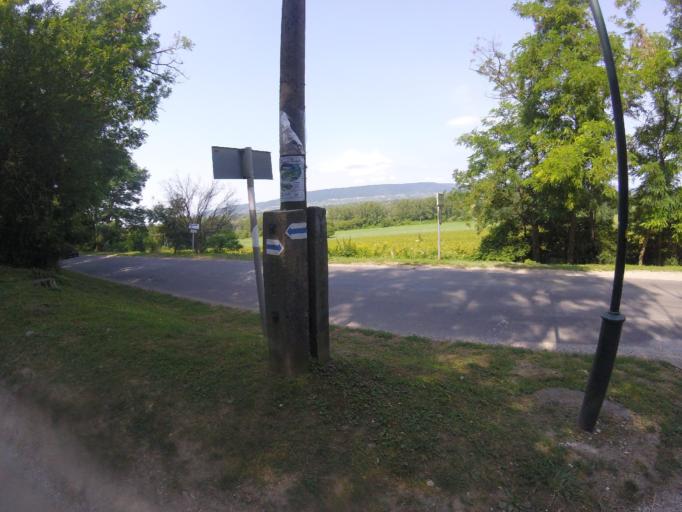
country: HU
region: Veszprem
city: Tapolca
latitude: 46.8056
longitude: 17.4340
